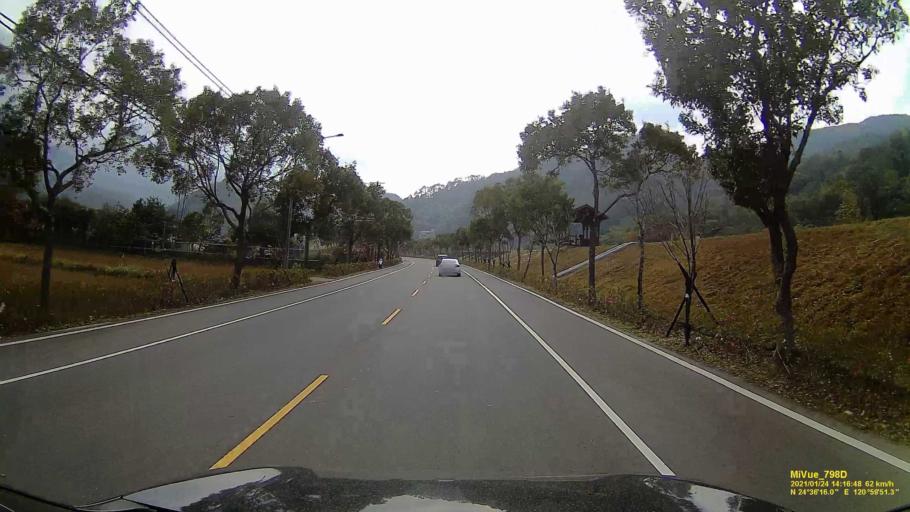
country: TW
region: Taiwan
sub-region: Miaoli
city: Miaoli
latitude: 24.6041
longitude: 120.9974
